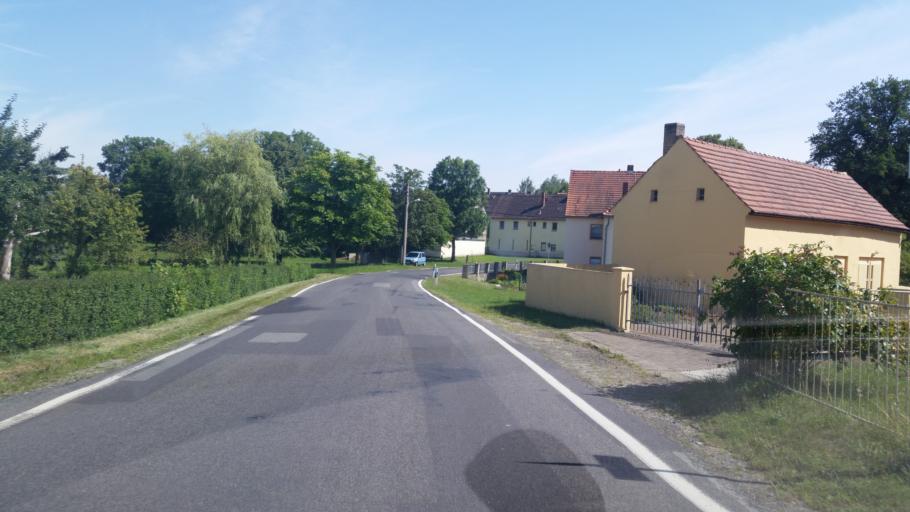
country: DE
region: Saxony
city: Schwepnitz
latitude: 51.3350
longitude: 14.0087
